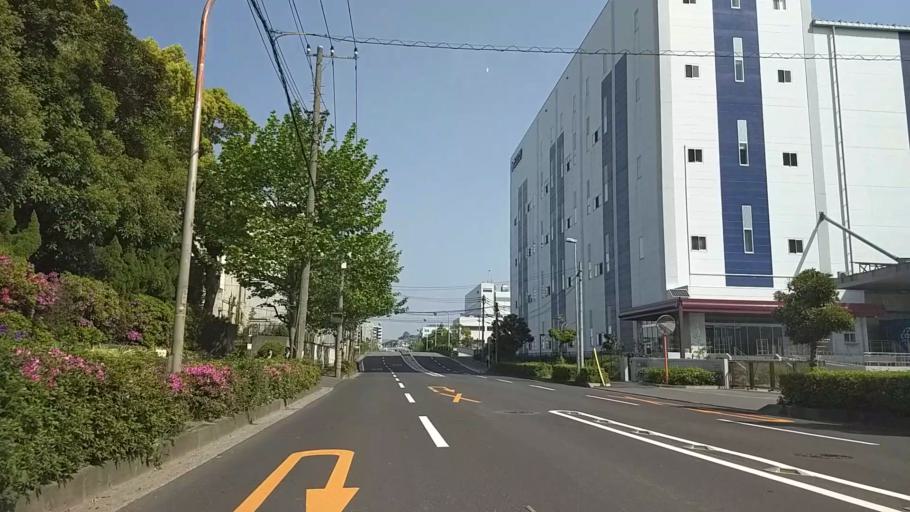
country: JP
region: Kanagawa
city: Yokohama
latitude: 35.4810
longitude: 139.6576
